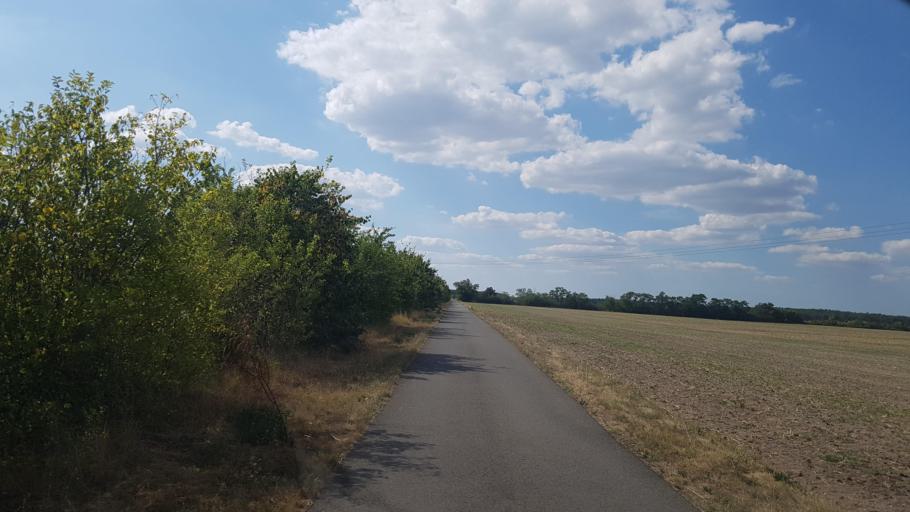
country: DE
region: Saxony-Anhalt
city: Elster
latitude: 51.8359
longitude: 12.8270
